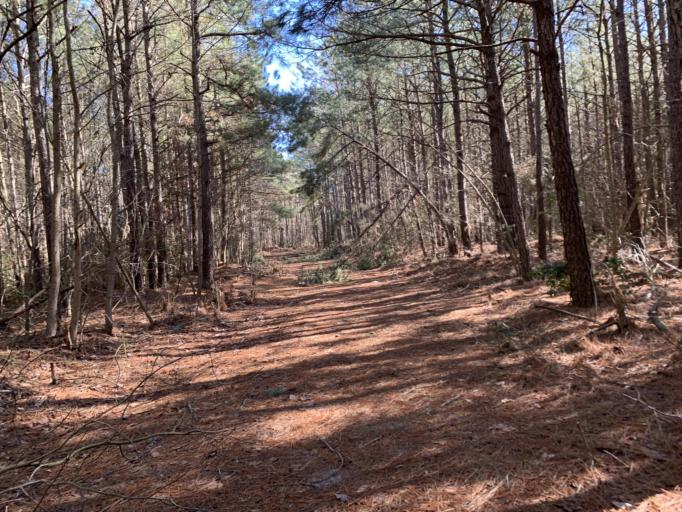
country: US
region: Delaware
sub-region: Sussex County
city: Georgetown
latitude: 38.6753
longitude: -75.4837
